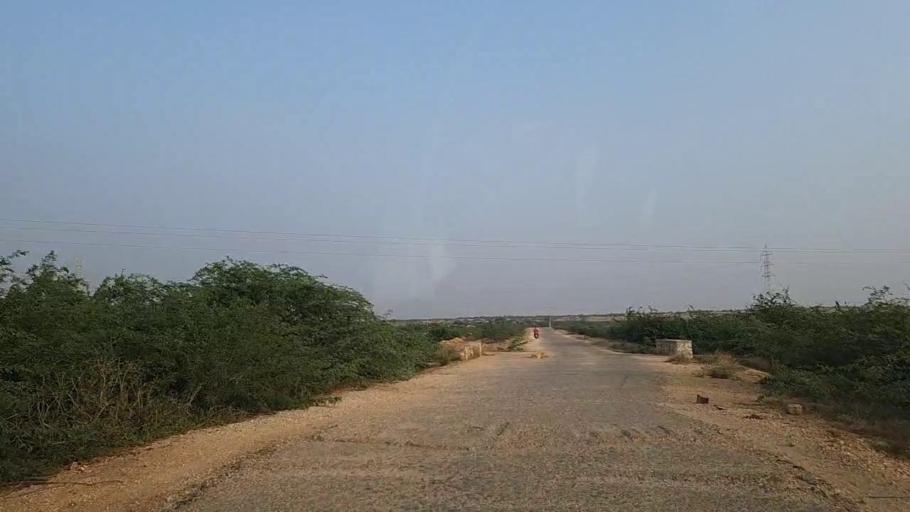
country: PK
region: Sindh
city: Thatta
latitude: 24.6895
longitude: 67.8497
